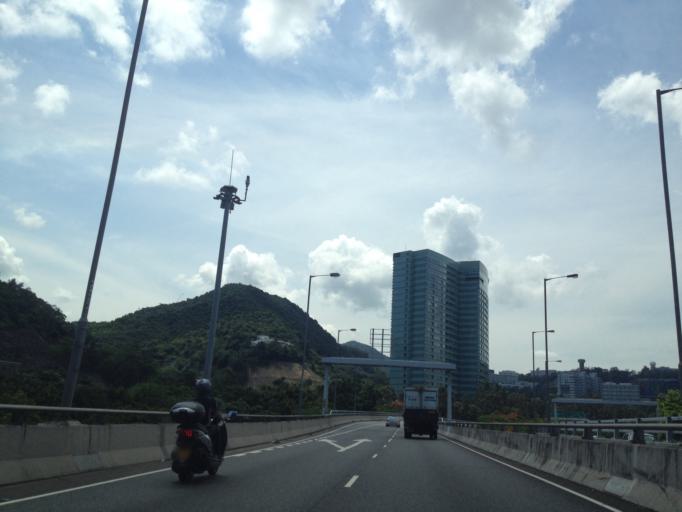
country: HK
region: Sha Tin
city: Sha Tin
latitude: 22.4093
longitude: 114.2138
